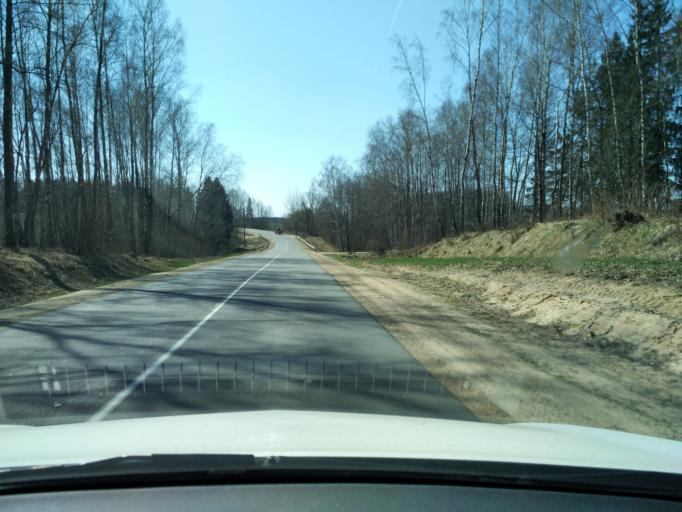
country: BY
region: Minsk
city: Slabada
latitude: 53.9900
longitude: 27.9619
